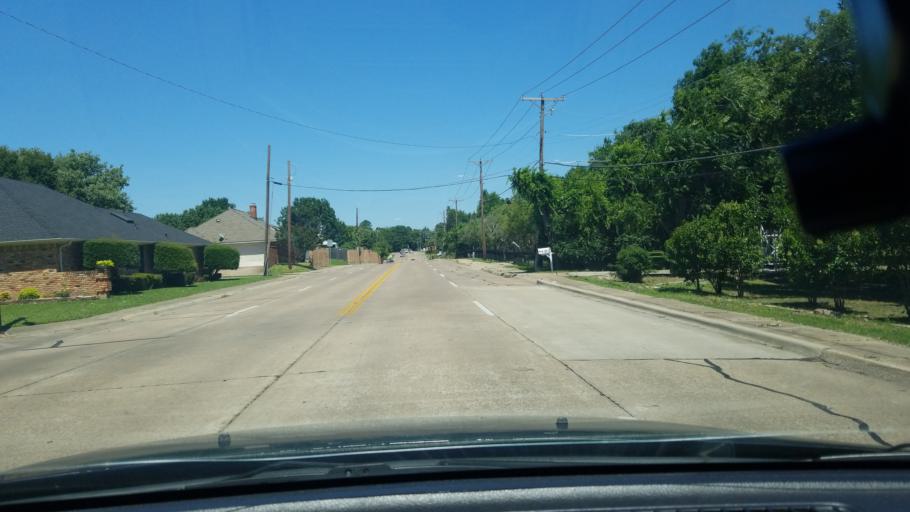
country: US
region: Texas
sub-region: Dallas County
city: Mesquite
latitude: 32.7559
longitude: -96.6012
